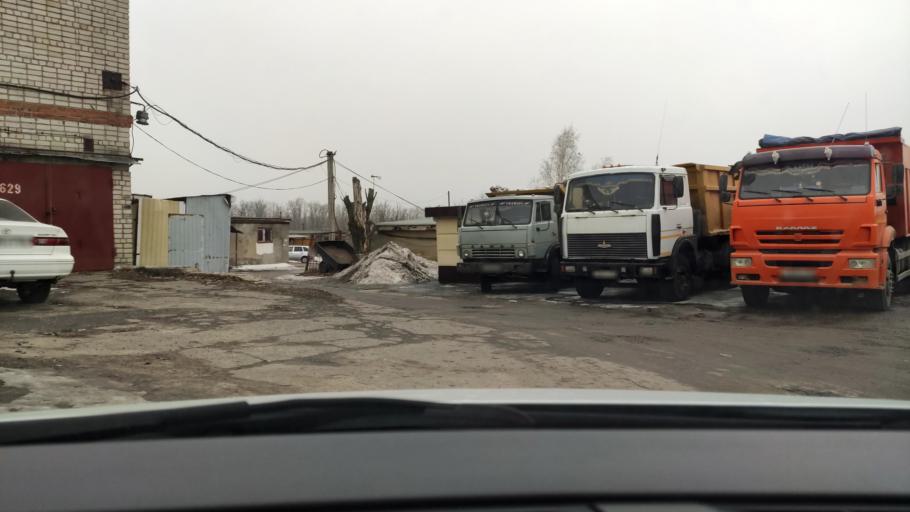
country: RU
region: Voronezj
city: Voronezh
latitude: 51.6387
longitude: 39.1333
